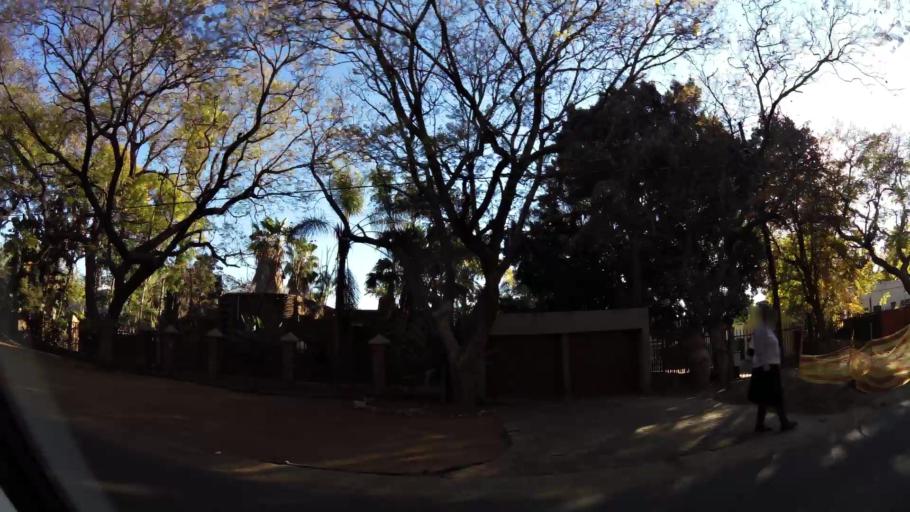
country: ZA
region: Limpopo
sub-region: Capricorn District Municipality
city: Polokwane
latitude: -23.9031
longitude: 29.4567
